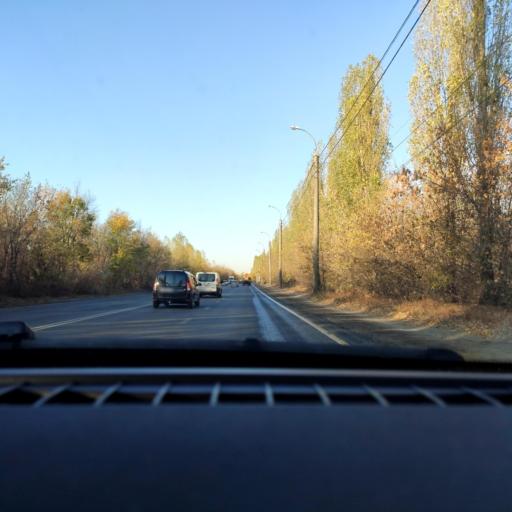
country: RU
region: Voronezj
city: Maslovka
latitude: 51.6032
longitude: 39.2540
